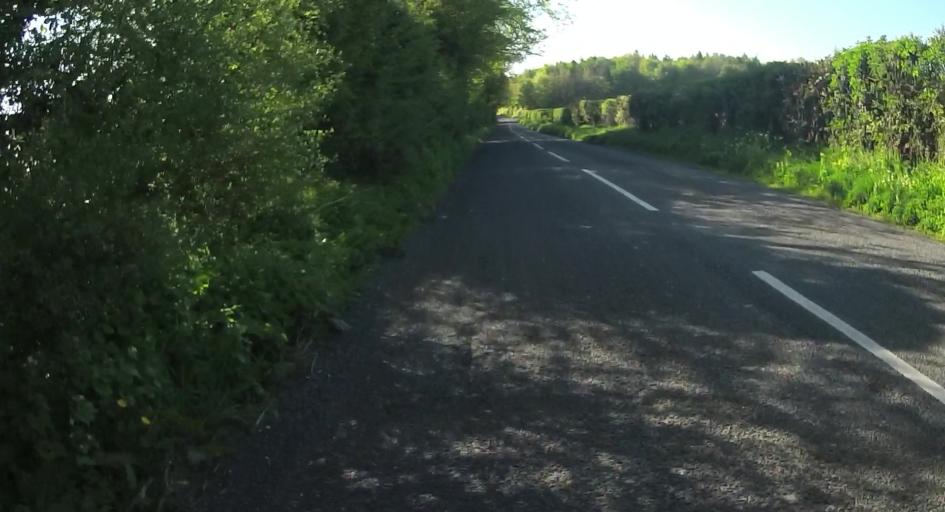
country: GB
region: England
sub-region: Hampshire
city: Old Basing
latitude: 51.2487
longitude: -1.0560
